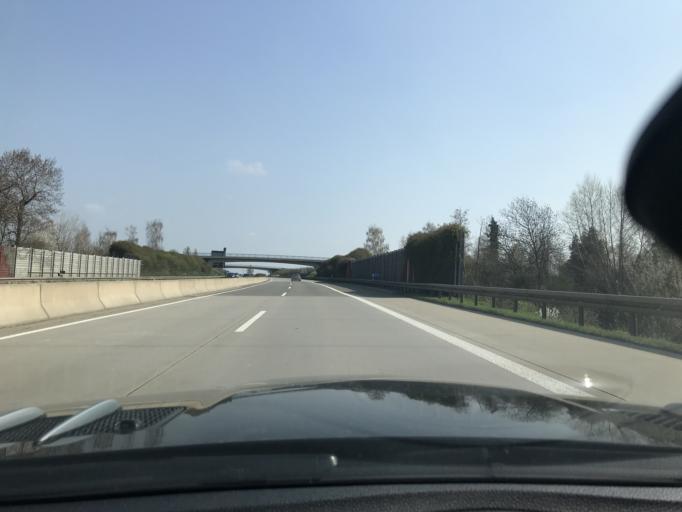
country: DE
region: Thuringia
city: Noda
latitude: 51.0337
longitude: 11.0073
